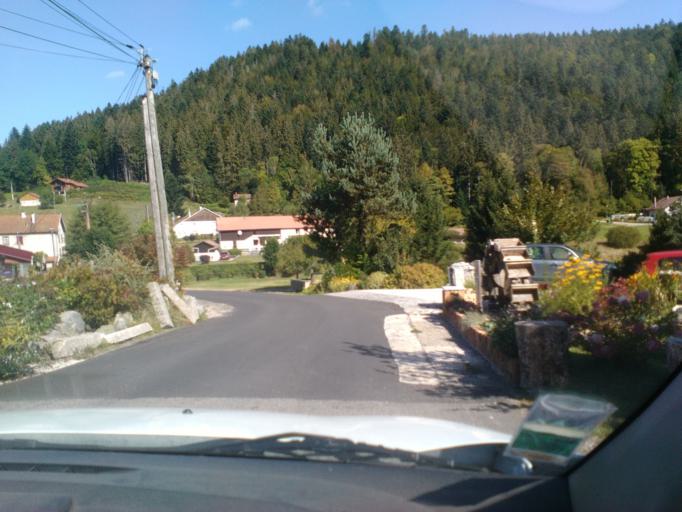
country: FR
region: Lorraine
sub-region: Departement des Vosges
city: Le Tholy
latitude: 48.0765
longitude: 6.7944
